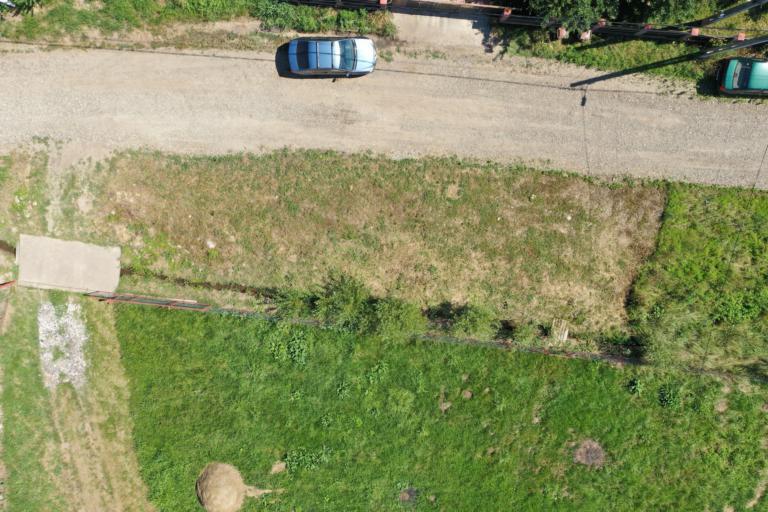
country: RO
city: Vanatori
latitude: 47.2529
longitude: 27.5218
